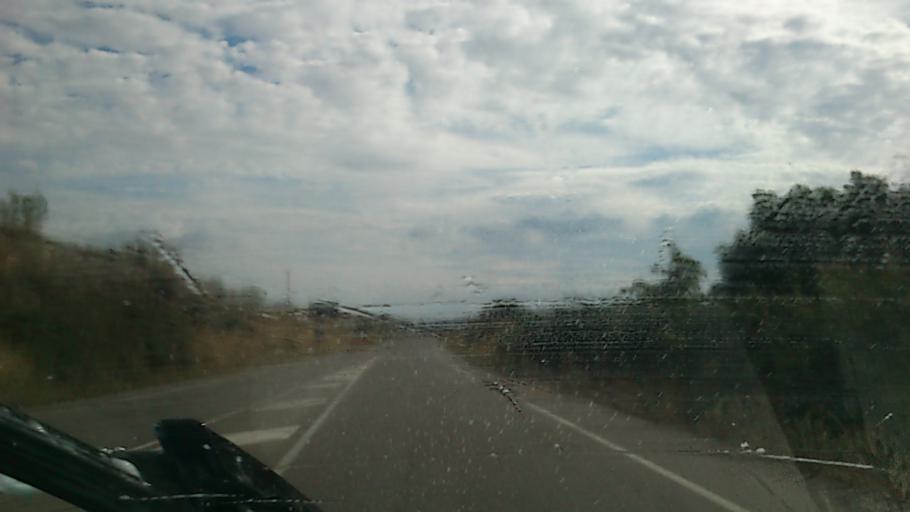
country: ES
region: Aragon
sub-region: Provincia de Zaragoza
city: San Mateo de Gallego
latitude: 41.8105
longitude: -0.7757
